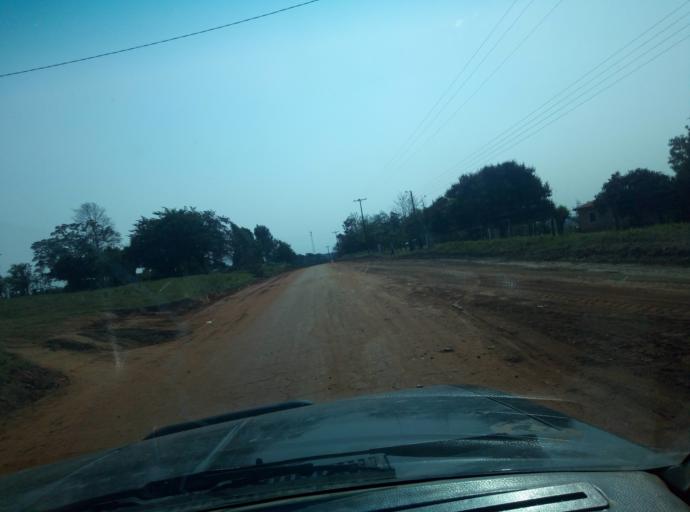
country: PY
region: Caaguazu
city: Carayao
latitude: -25.3234
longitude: -56.3297
